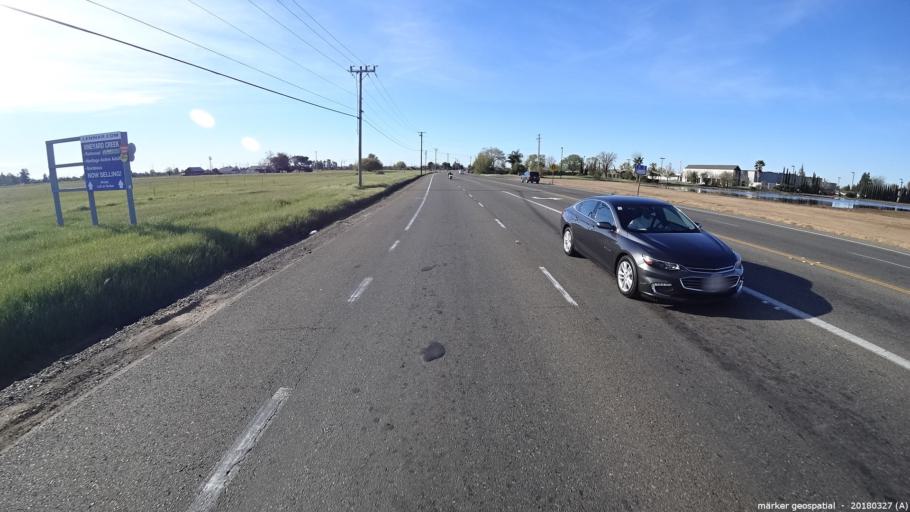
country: US
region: California
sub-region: Sacramento County
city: Florin
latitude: 38.4958
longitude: -121.3721
